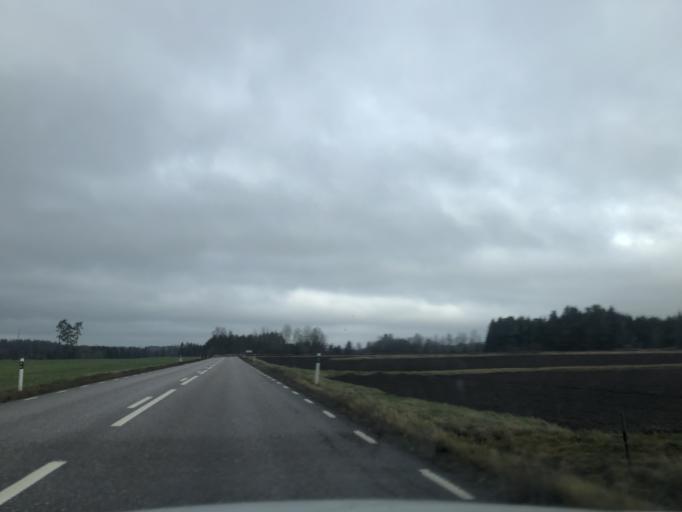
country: SE
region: Vaestra Goetaland
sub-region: Ulricehamns Kommun
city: Ulricehamn
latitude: 57.8725
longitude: 13.4326
